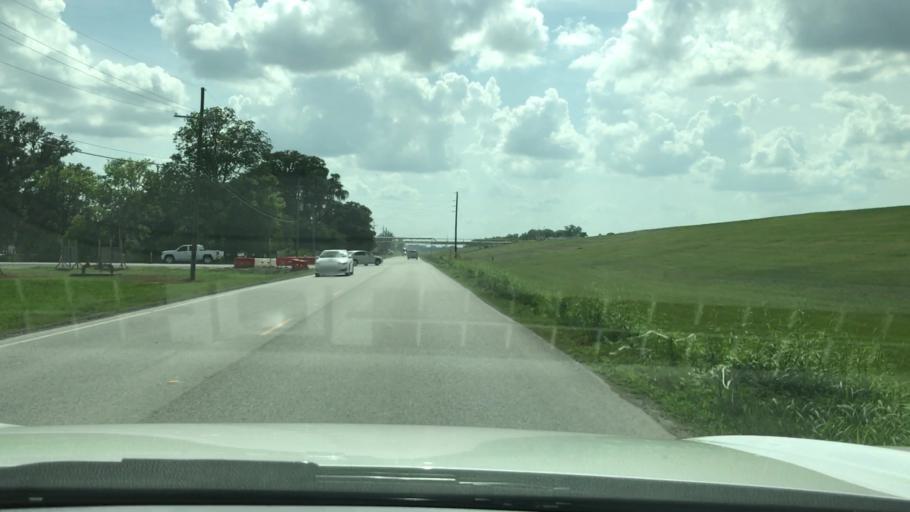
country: US
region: Louisiana
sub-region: Iberville Parish
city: Plaquemine
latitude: 30.2734
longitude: -91.1770
